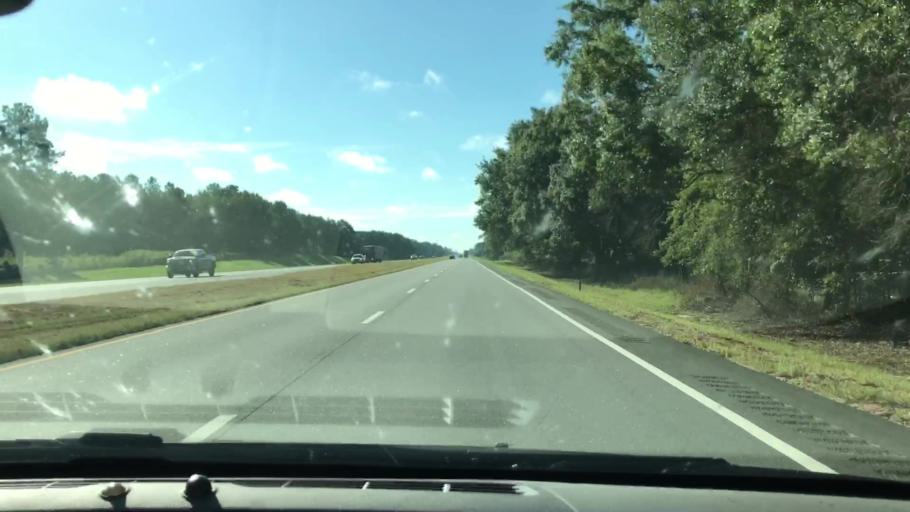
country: US
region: Georgia
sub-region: Lee County
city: Leesburg
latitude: 31.6788
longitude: -84.2981
